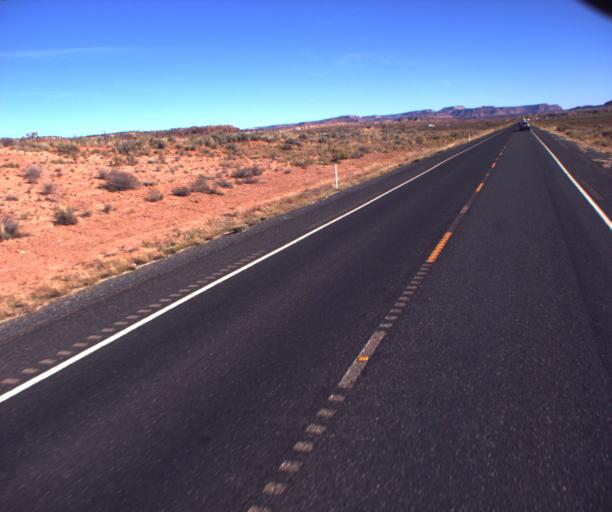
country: US
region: Arizona
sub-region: Coconino County
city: Fredonia
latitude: 36.9355
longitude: -112.5544
